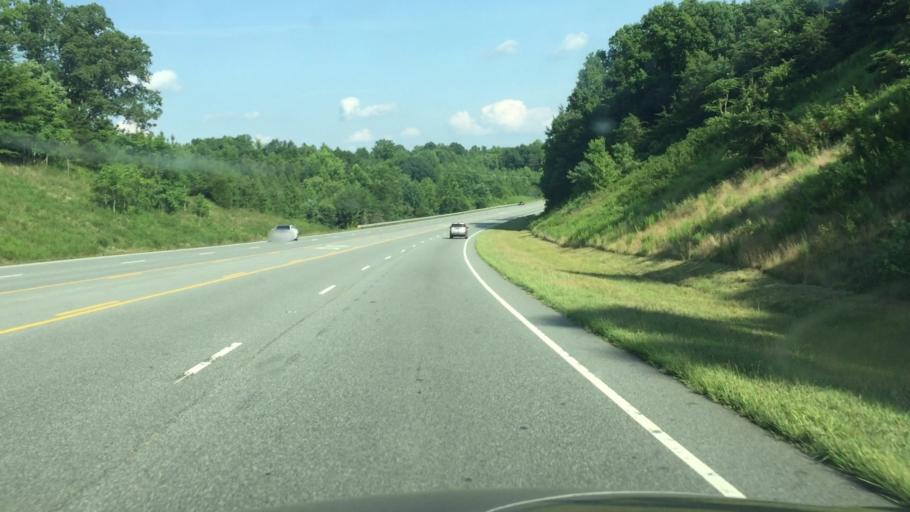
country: US
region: North Carolina
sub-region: Rockingham County
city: Reidsville
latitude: 36.3735
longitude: -79.6502
